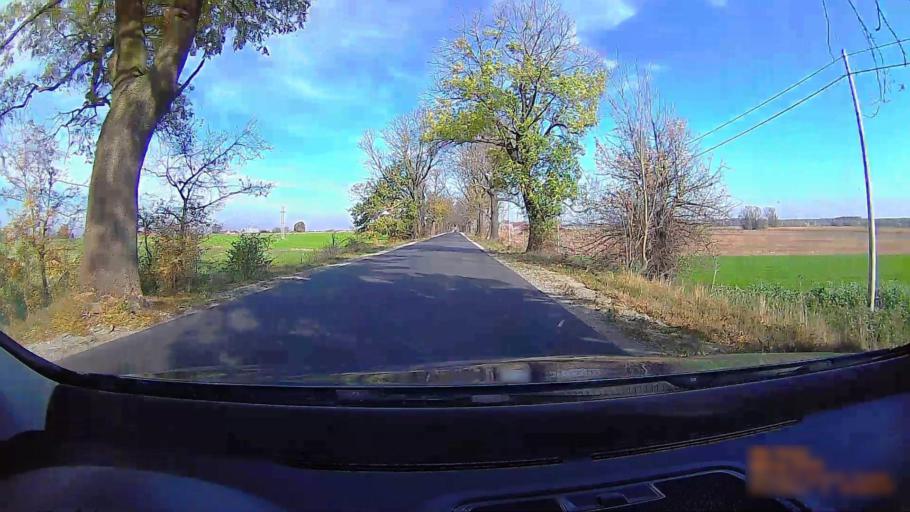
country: PL
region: Greater Poland Voivodeship
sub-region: Powiat ostrzeszowski
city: Doruchow
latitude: 51.3981
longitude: 18.0618
